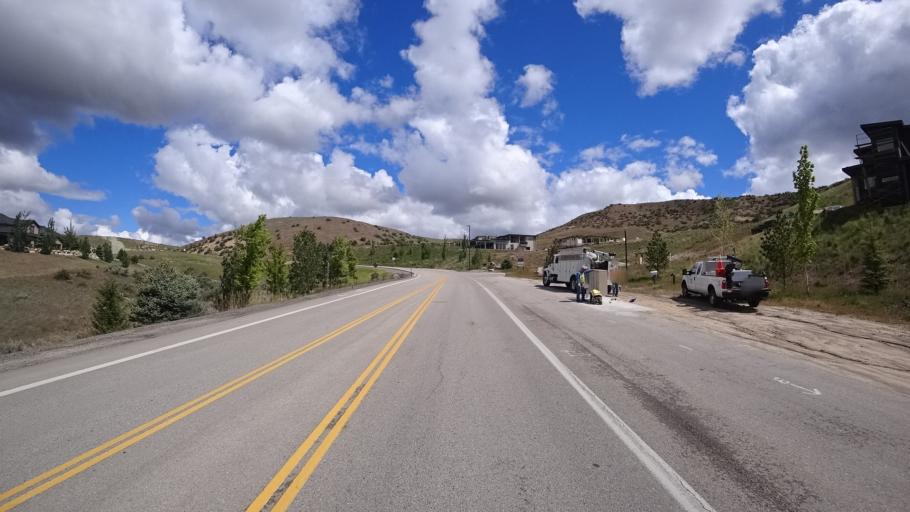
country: US
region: Idaho
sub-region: Ada County
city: Boise
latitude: 43.6608
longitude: -116.1899
